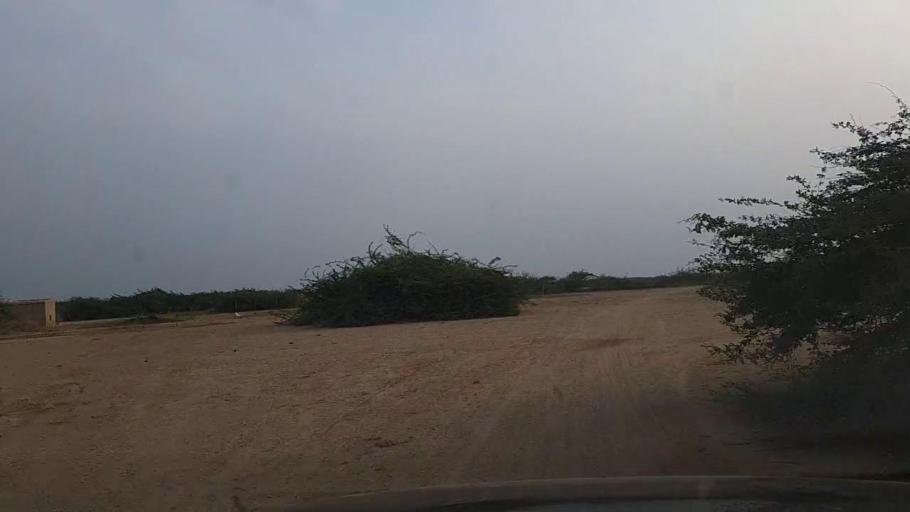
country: PK
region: Sindh
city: Gharo
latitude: 24.7754
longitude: 67.7071
